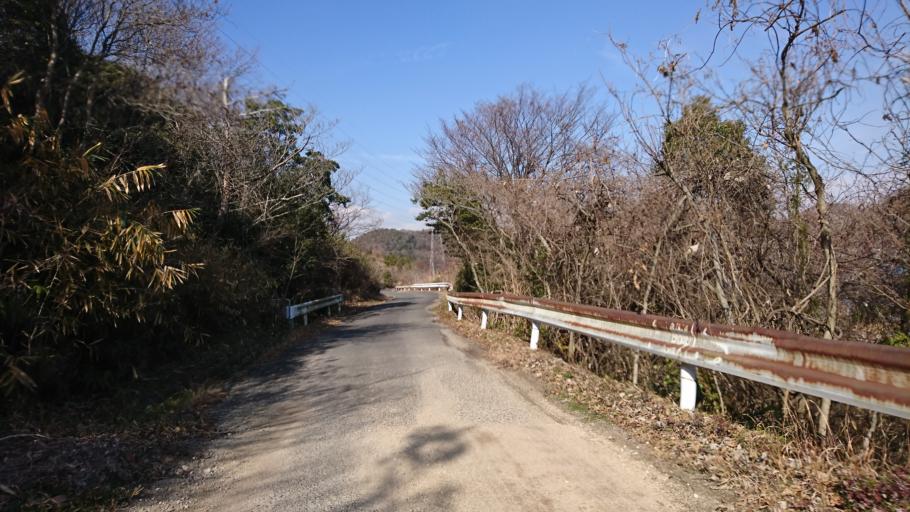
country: JP
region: Hyogo
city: Ono
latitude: 34.8279
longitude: 134.8736
